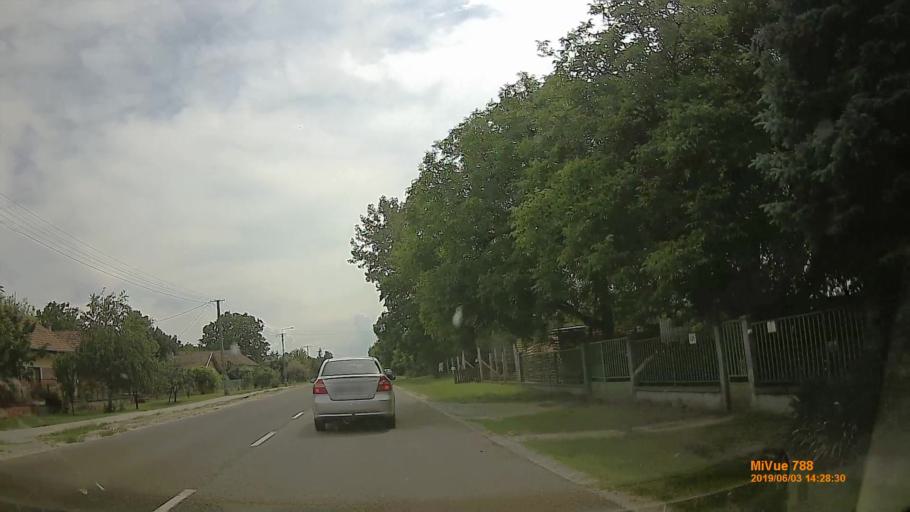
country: HU
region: Bacs-Kiskun
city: Tiszakecske
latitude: 46.9779
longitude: 20.1133
